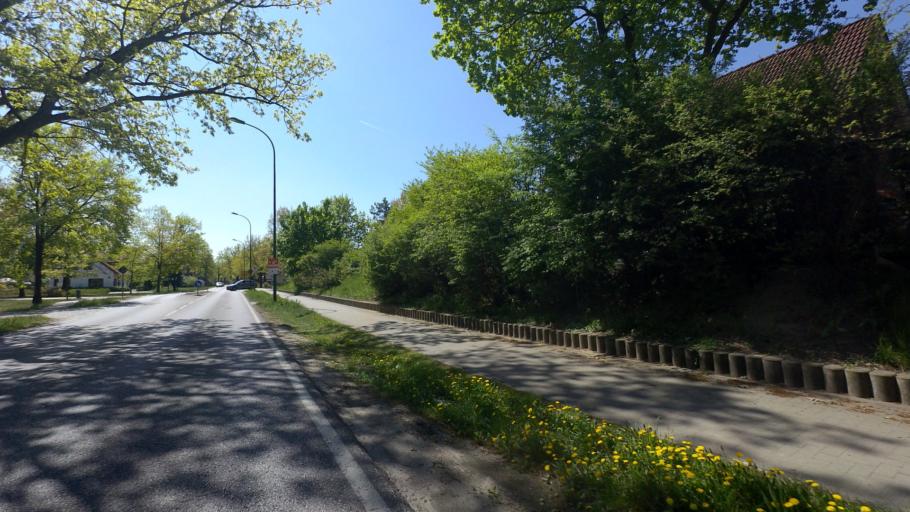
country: DE
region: Brandenburg
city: Bestensee
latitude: 52.2655
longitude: 13.6340
